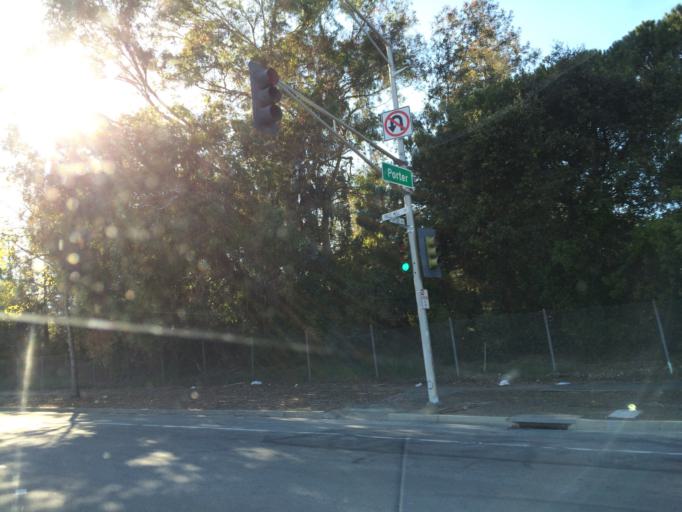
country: US
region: California
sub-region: Santa Clara County
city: Stanford
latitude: 37.4095
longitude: -122.1532
